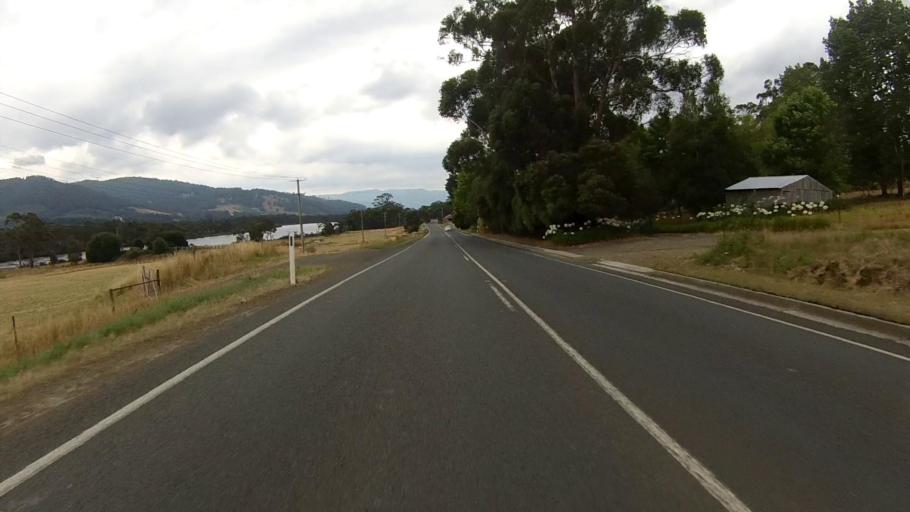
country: AU
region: Tasmania
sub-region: Huon Valley
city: Franklin
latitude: -43.0858
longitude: 147.0296
